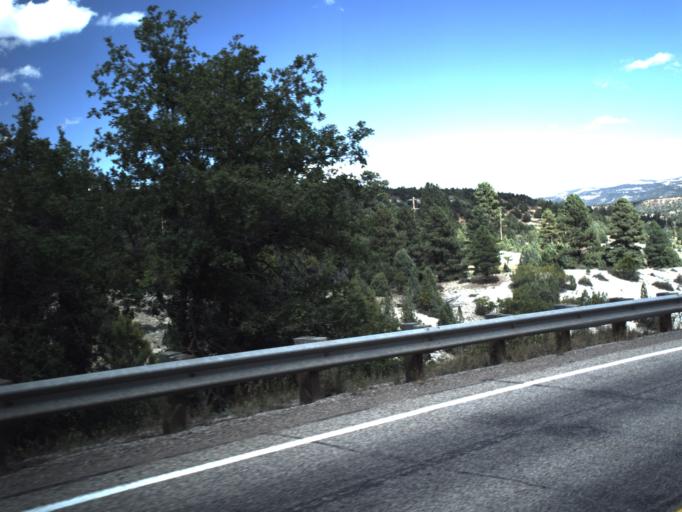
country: US
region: Utah
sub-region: Garfield County
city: Panguitch
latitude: 37.4912
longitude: -112.5229
